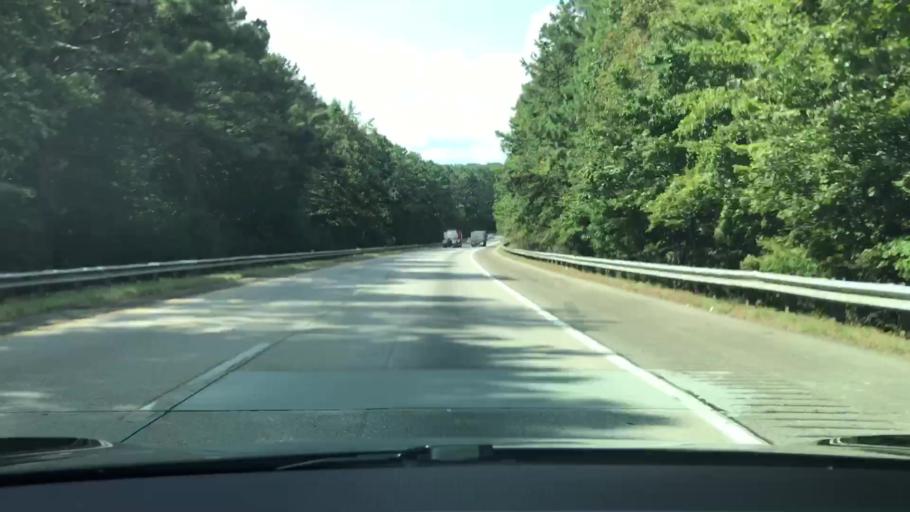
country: US
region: Georgia
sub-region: Hall County
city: Oakwood
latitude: 34.2393
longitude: -83.8416
